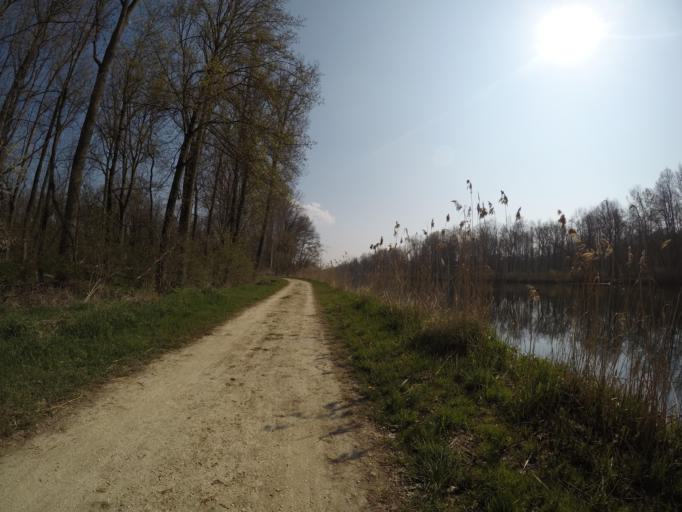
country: DE
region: Bavaria
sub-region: Swabia
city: Leipheim
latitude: 48.4563
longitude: 10.2279
